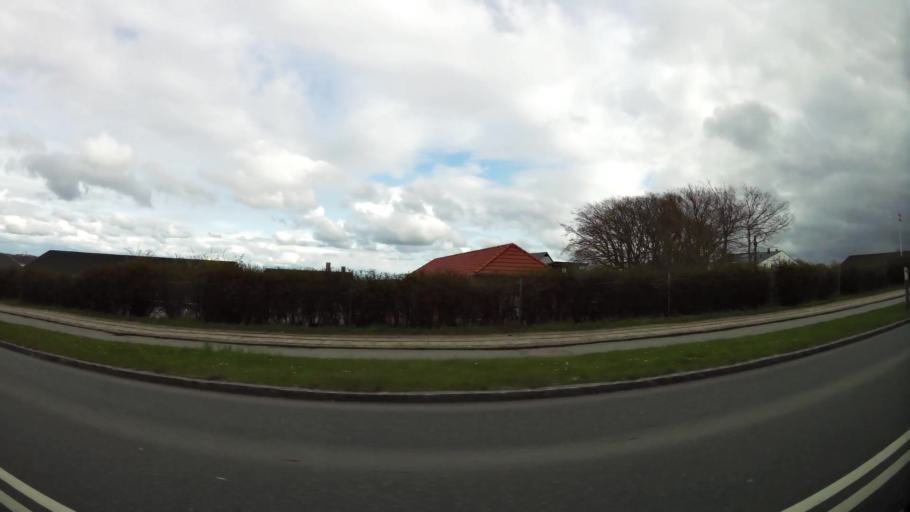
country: DK
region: North Denmark
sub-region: Thisted Kommune
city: Thisted
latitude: 56.9482
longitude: 8.6621
